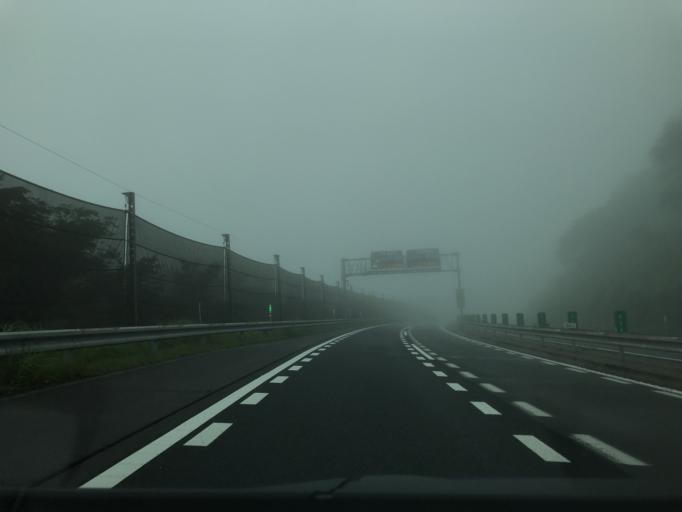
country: JP
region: Oita
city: Hiji
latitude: 33.3590
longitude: 131.4500
